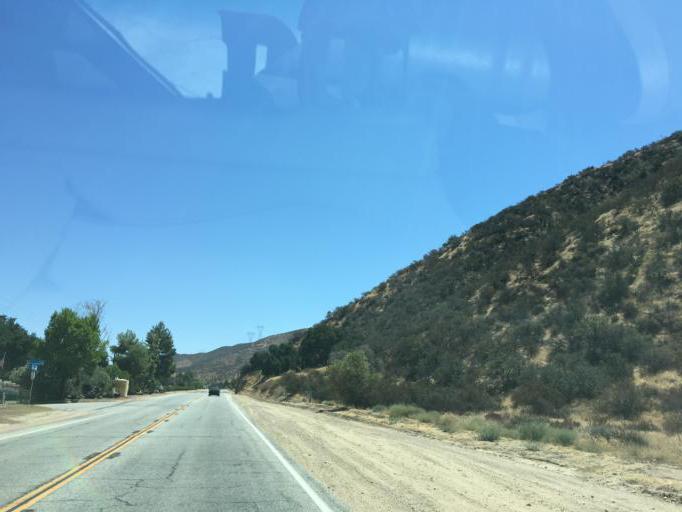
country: US
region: California
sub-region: Los Angeles County
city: Agua Dulce
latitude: 34.5109
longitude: -118.3538
